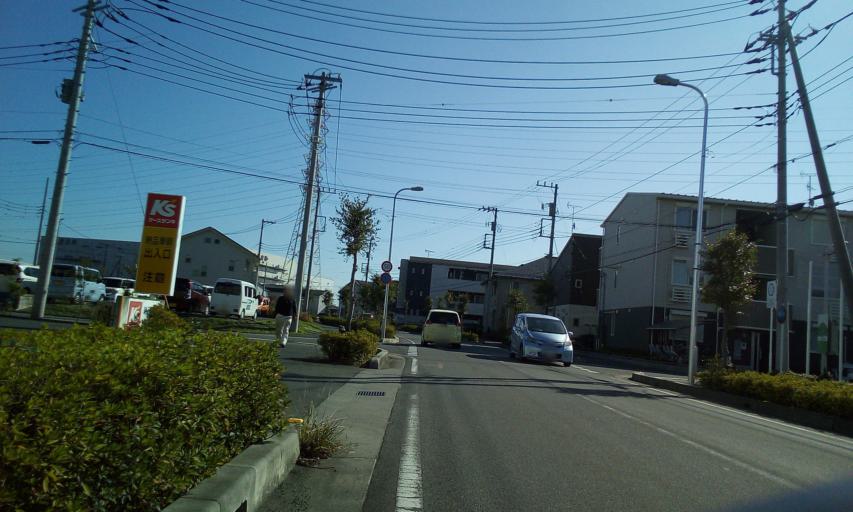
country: JP
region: Saitama
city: Yoshikawa
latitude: 35.8653
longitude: 139.8570
